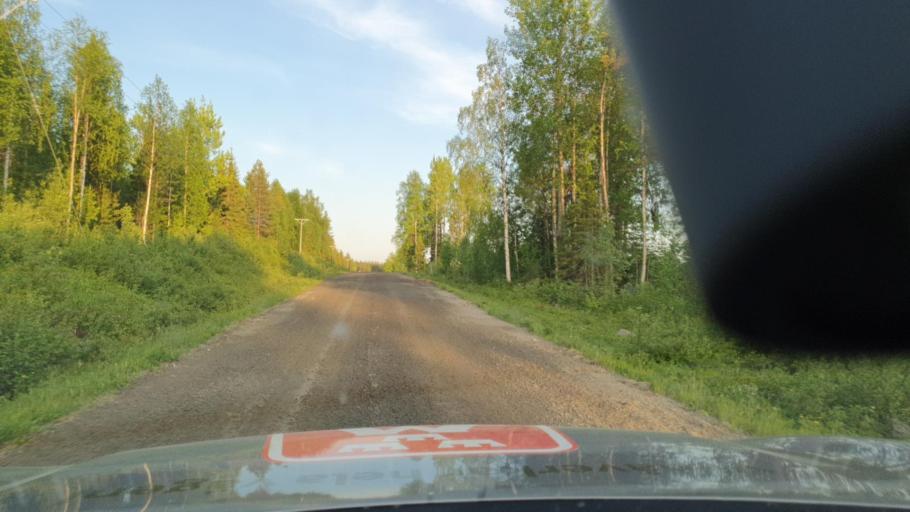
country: SE
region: Norrbotten
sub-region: Bodens Kommun
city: Boden
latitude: 66.1139
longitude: 21.5601
